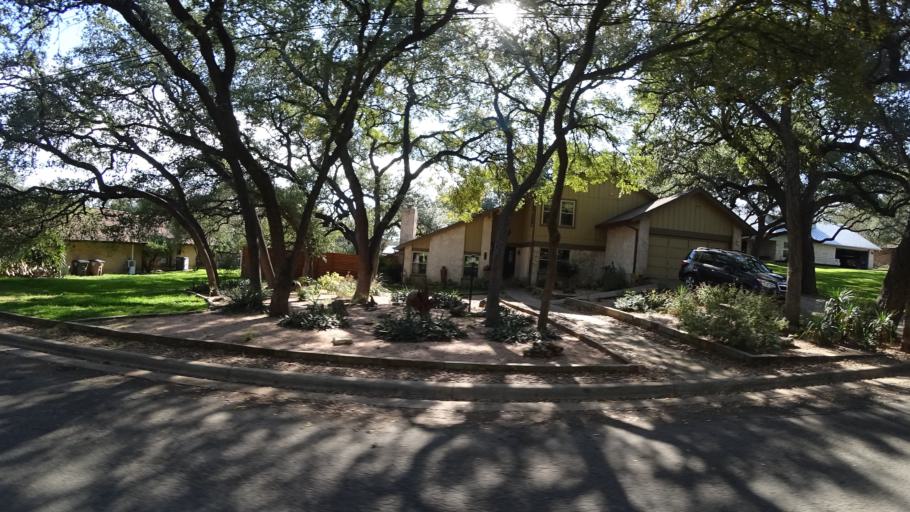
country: US
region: Texas
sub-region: Travis County
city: Shady Hollow
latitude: 30.2216
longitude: -97.9091
